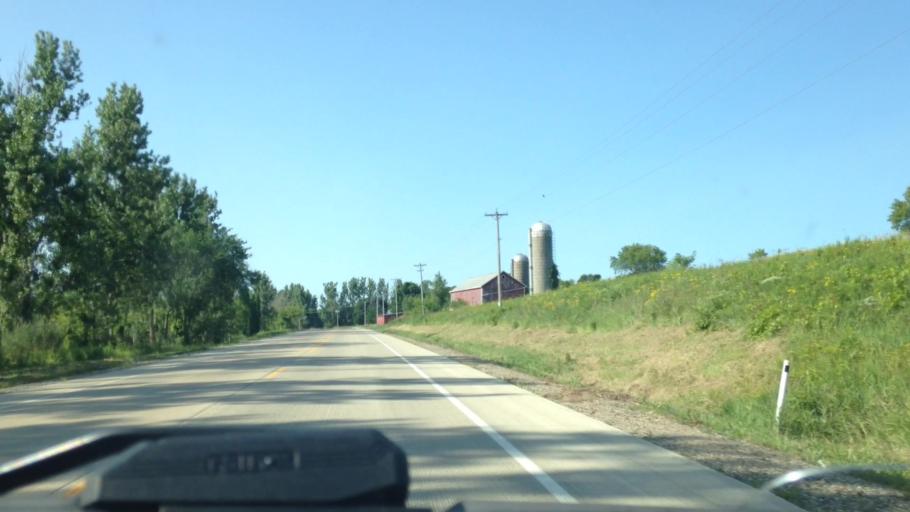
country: US
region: Wisconsin
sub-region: Dodge County
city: Mayville
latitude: 43.4682
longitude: -88.5599
